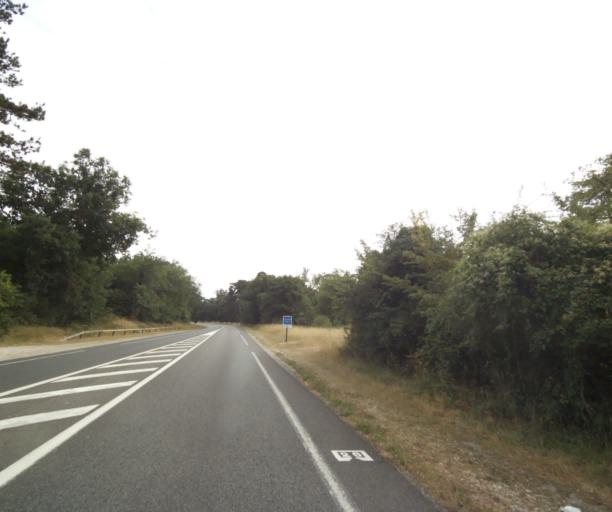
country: FR
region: Ile-de-France
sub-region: Departement de Seine-et-Marne
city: Bois-le-Roi
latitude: 48.4399
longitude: 2.6902
